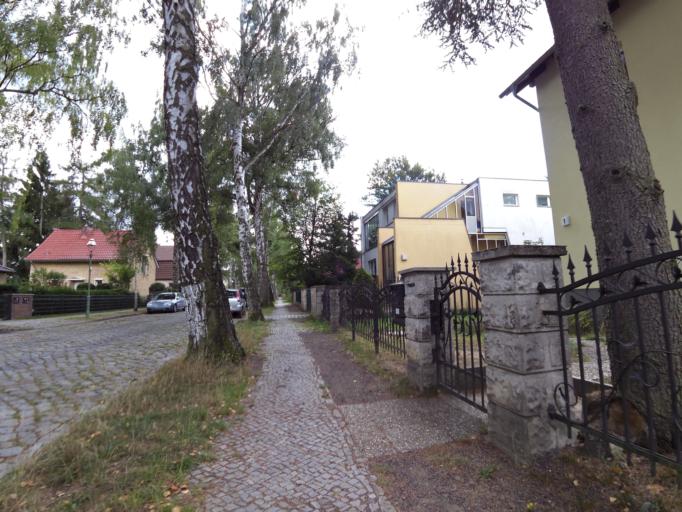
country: DE
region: Berlin
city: Lichtenrade
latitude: 52.3863
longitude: 13.3887
